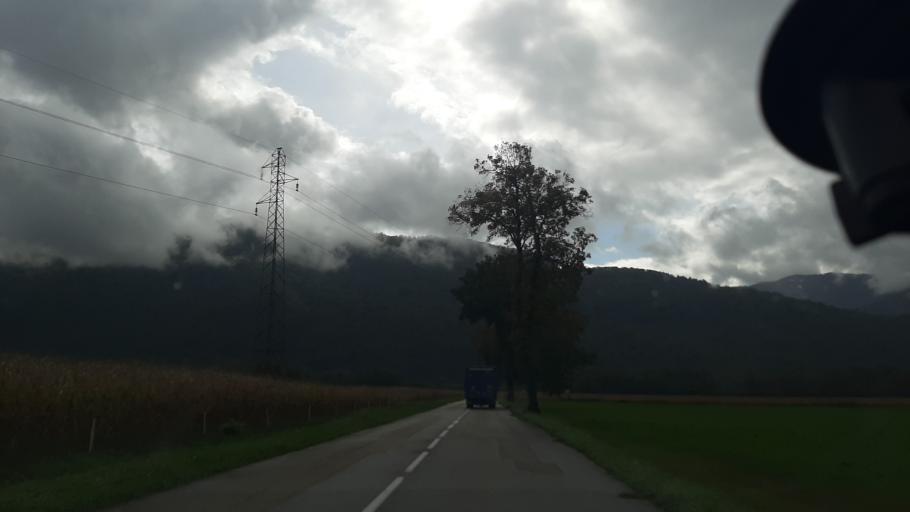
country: FR
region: Rhone-Alpes
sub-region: Departement de la Savoie
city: Gresy-sur-Isere
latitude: 45.5902
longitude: 6.2647
